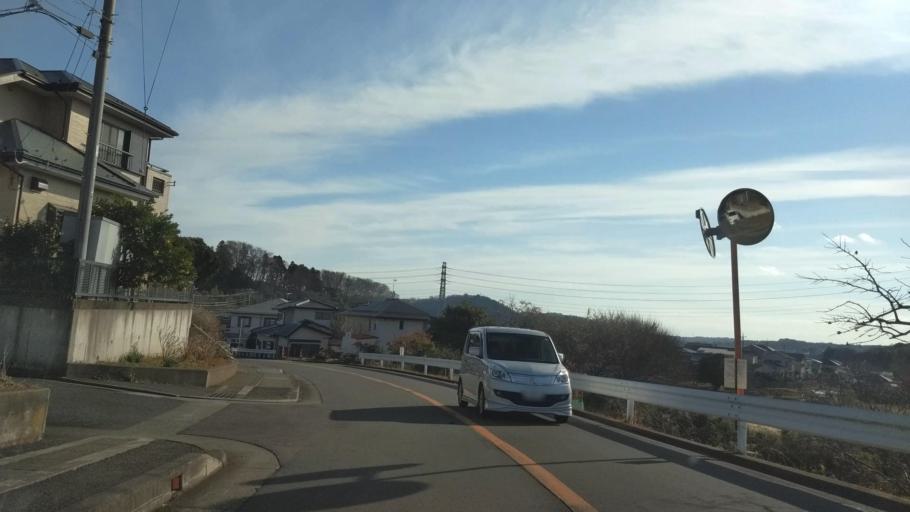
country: JP
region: Kanagawa
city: Hadano
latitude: 35.3933
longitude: 139.2345
